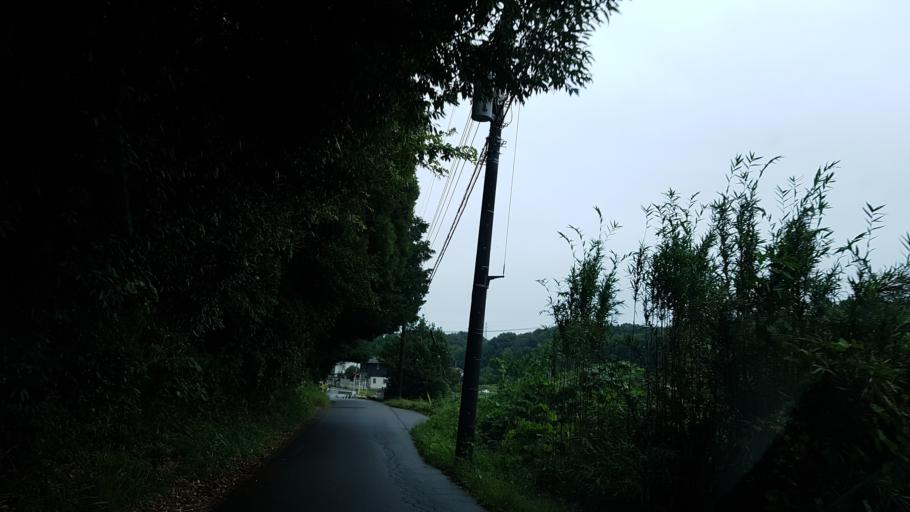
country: JP
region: Tochigi
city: Utsunomiya-shi
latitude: 36.5983
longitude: 139.8815
